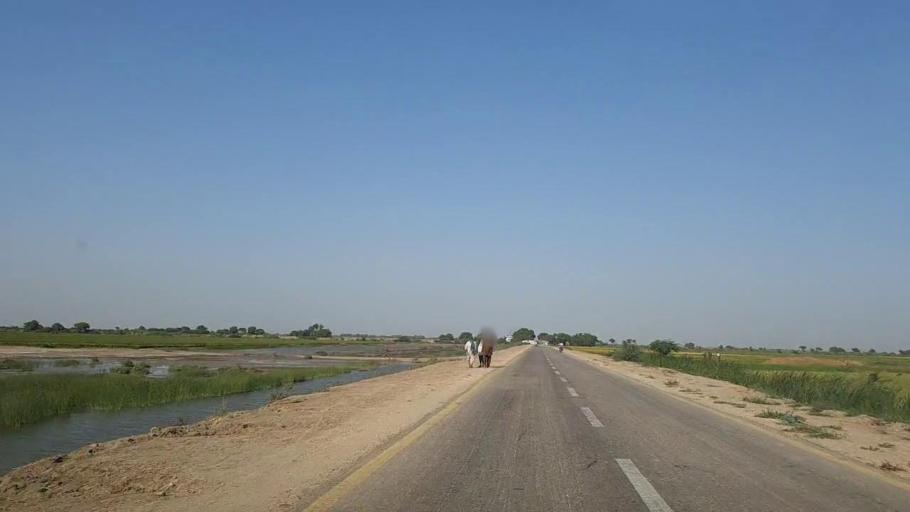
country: PK
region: Sindh
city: Jati
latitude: 24.4120
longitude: 68.3006
